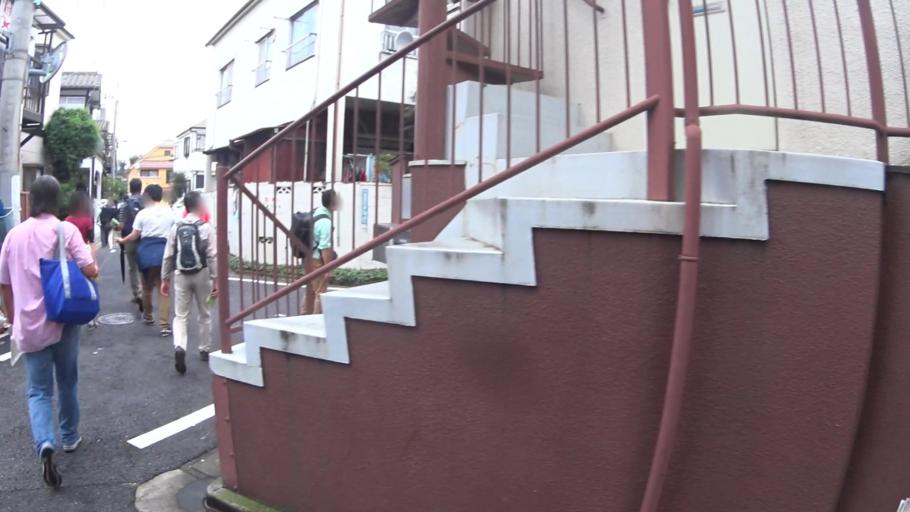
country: JP
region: Tokyo
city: Tokyo
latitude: 35.7370
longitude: 139.6807
